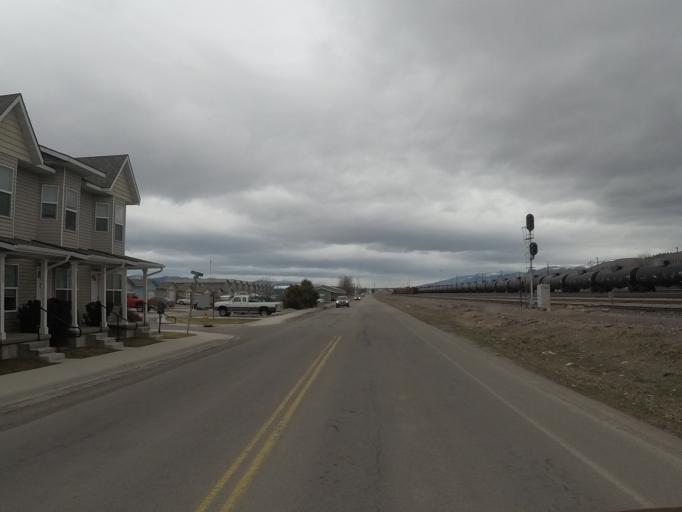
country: US
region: Montana
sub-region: Missoula County
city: Missoula
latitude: 46.8891
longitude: -114.0200
